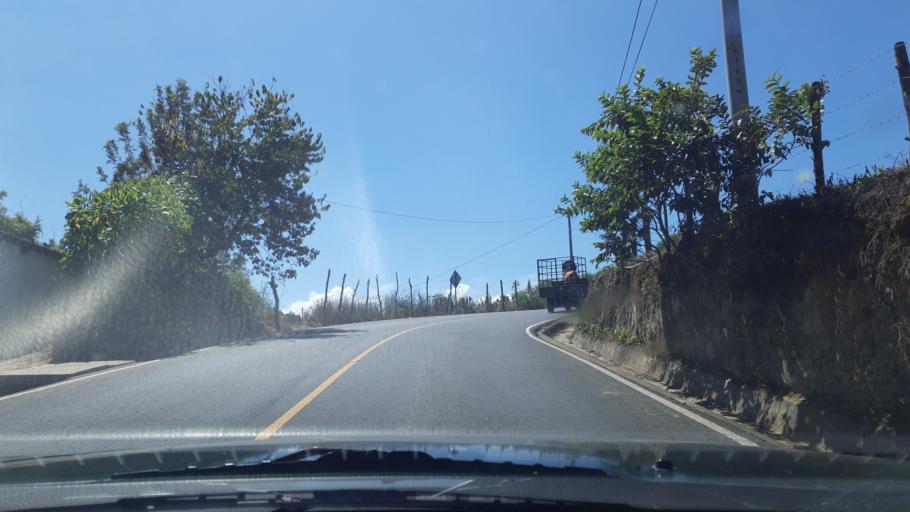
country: GT
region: Chimaltenango
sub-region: Municipio de Zaragoza
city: Zaragoza
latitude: 14.6658
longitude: -90.8610
